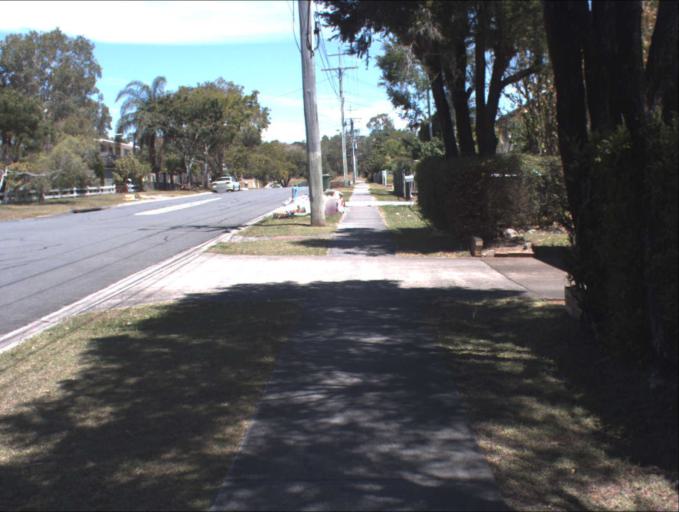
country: AU
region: Queensland
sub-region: Logan
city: Logan City
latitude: -27.6459
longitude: 153.1211
